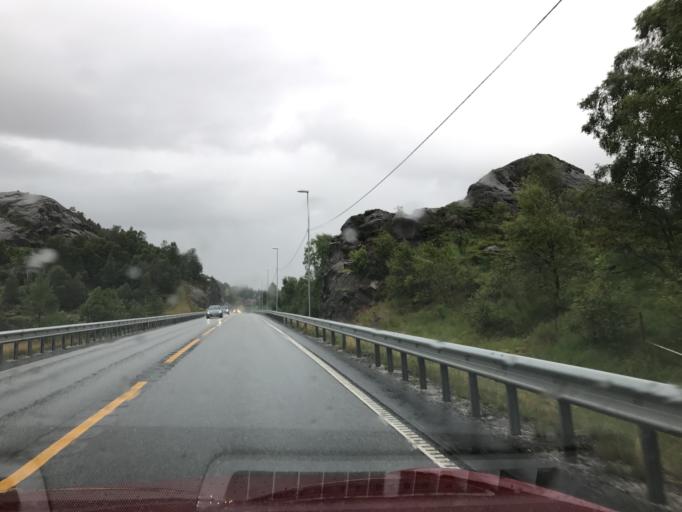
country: NO
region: Rogaland
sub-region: Bjerkreim
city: Vikesa
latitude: 58.5463
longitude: 6.0632
